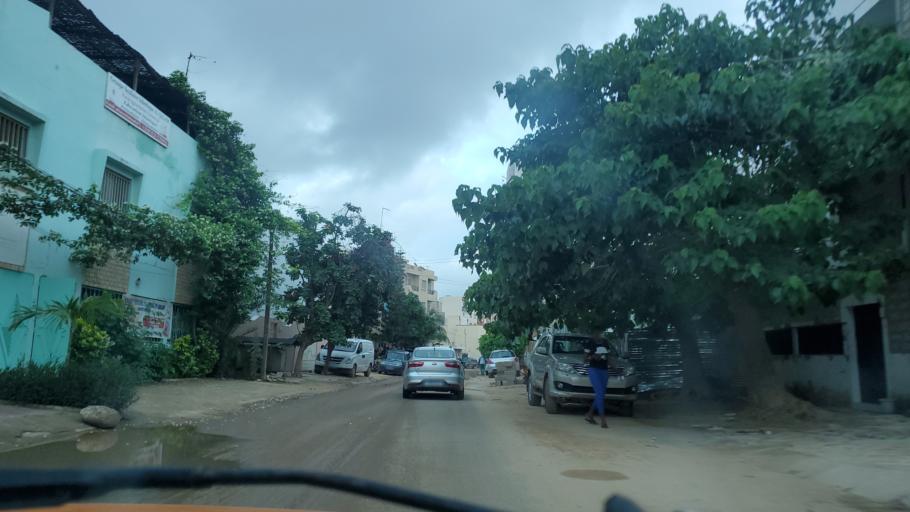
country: SN
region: Dakar
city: Mermoz Boabab
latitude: 14.7179
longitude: -17.4697
